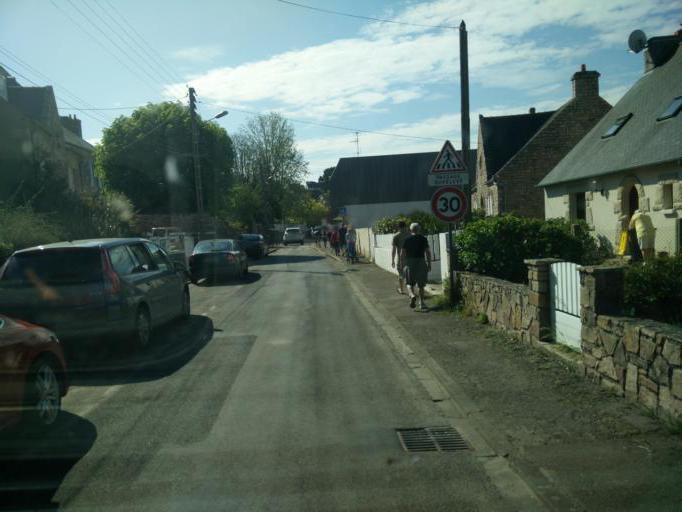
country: FR
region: Brittany
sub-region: Departement des Cotes-d'Armor
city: Erquy
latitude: 48.6312
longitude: -2.4624
